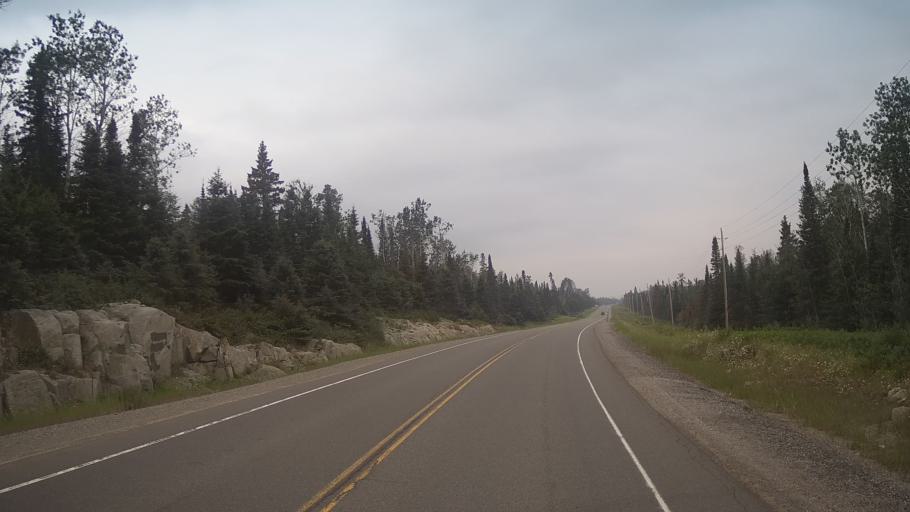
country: CA
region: Ontario
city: Greenstone
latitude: 49.5334
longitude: -88.0064
